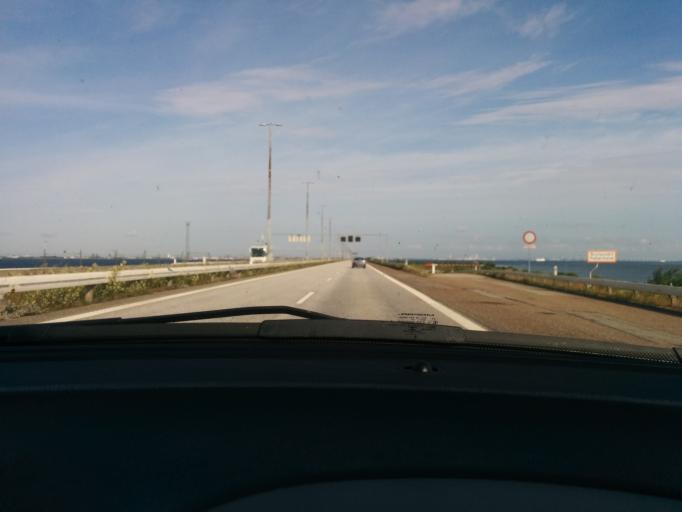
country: DK
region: Capital Region
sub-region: Dragor Kommune
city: Dragor
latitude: 55.5984
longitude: 12.7553
